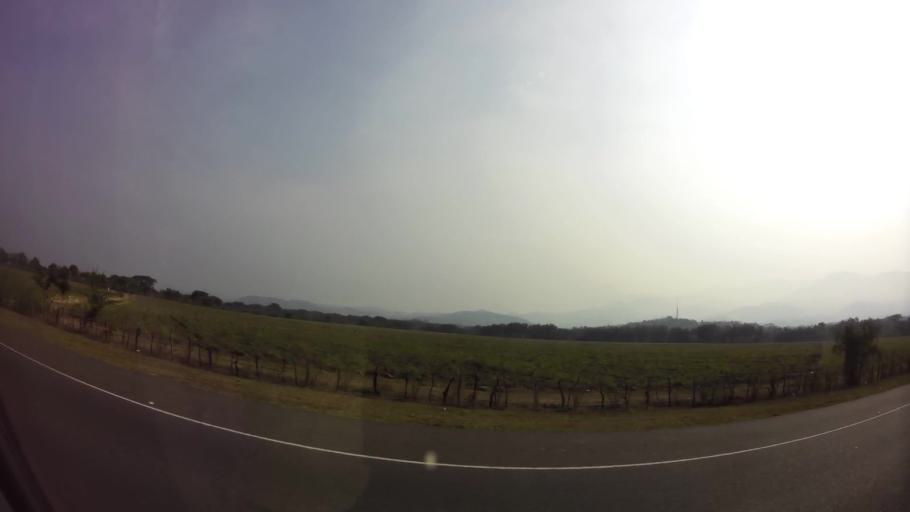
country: HN
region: Comayagua
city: Comayagua
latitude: 14.4345
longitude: -87.6523
